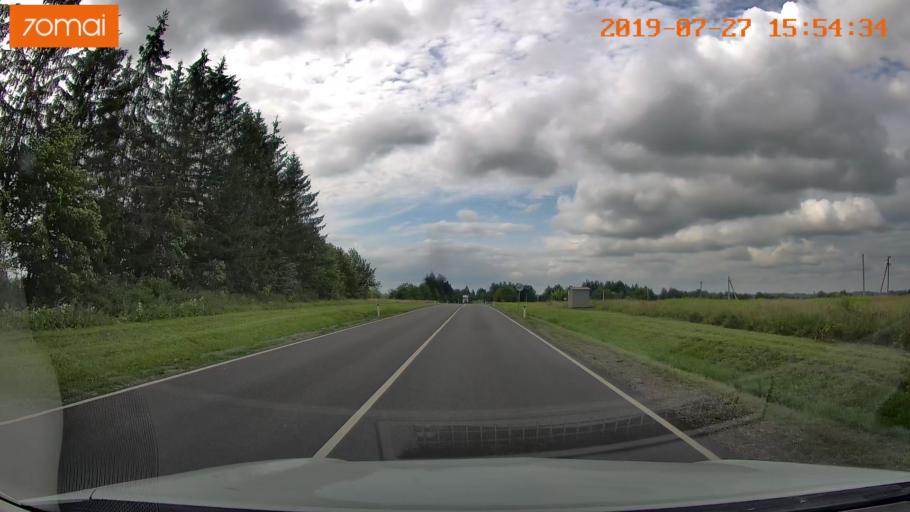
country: RU
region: Kaliningrad
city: Chernyakhovsk
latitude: 54.6083
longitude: 21.9372
